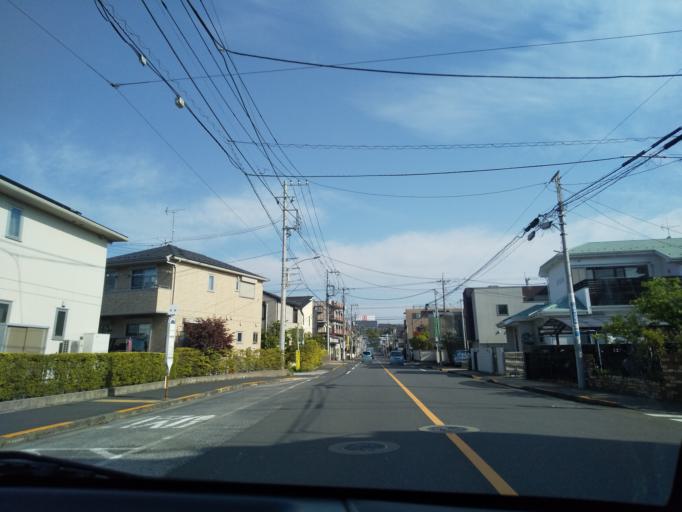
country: JP
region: Tokyo
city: Hino
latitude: 35.6689
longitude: 139.3849
